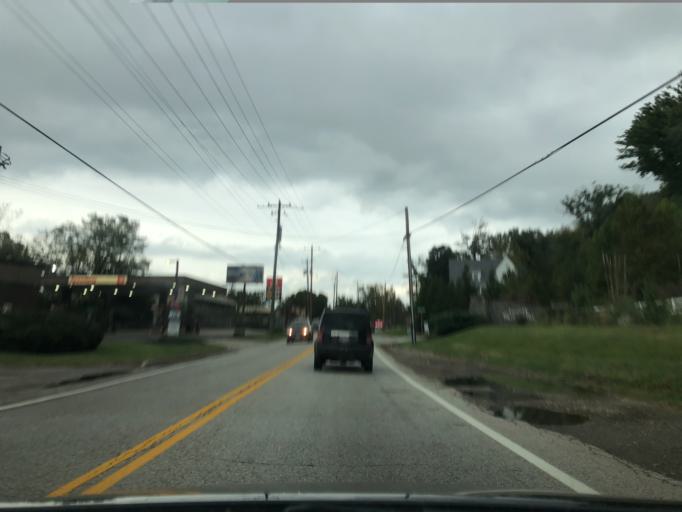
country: US
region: Ohio
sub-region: Hamilton County
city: Turpin Hills
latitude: 39.1101
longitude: -84.3991
